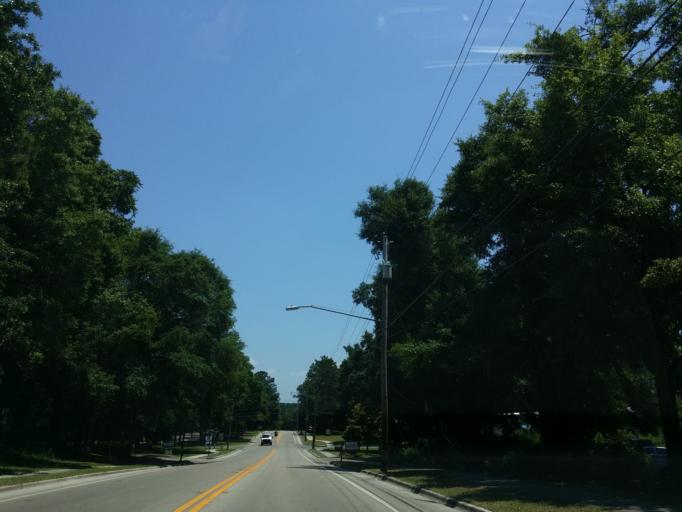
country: US
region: Florida
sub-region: Leon County
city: Tallahassee
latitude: 30.4691
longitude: -84.3557
